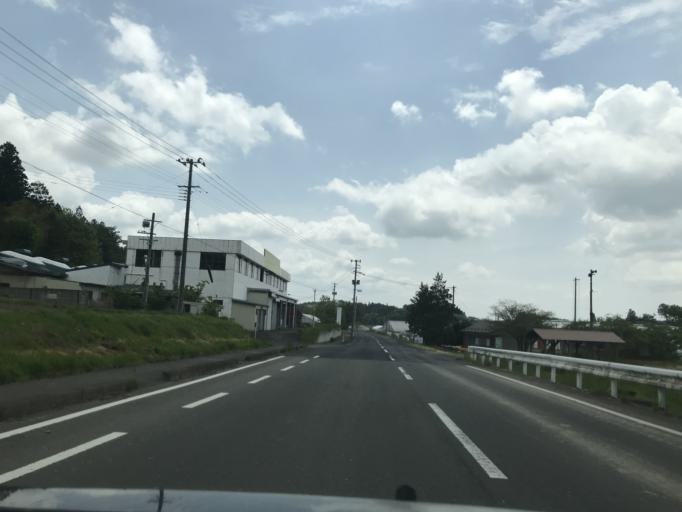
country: JP
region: Miyagi
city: Furukawa
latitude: 38.6860
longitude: 140.9536
